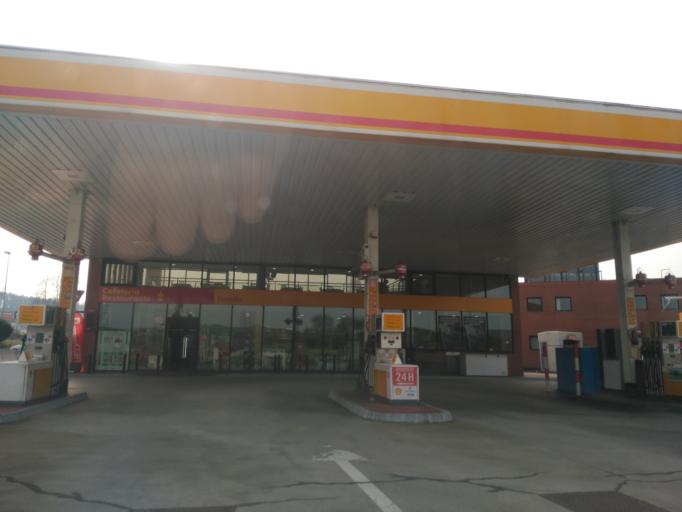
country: ES
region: Cantabria
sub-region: Provincia de Cantabria
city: Reocin
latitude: 43.3562
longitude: -4.0943
